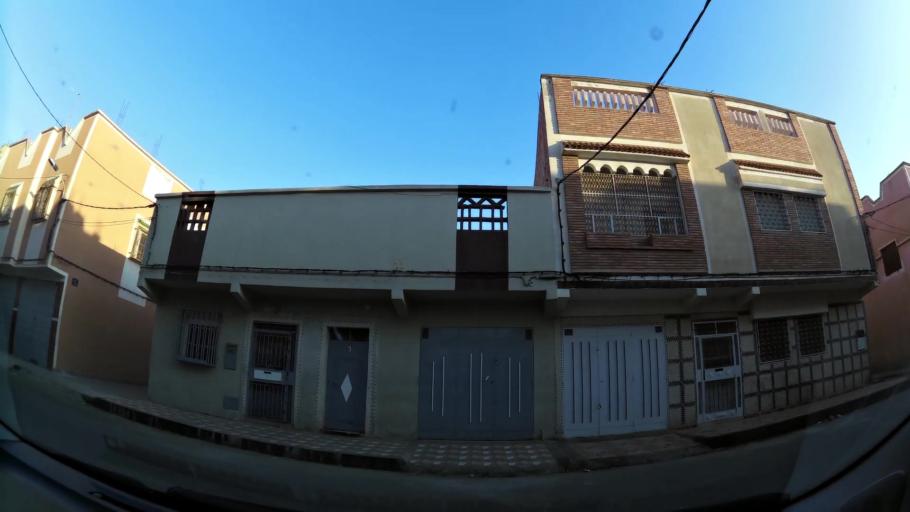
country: MA
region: Oriental
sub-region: Oujda-Angad
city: Oujda
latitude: 34.7091
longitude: -1.9121
